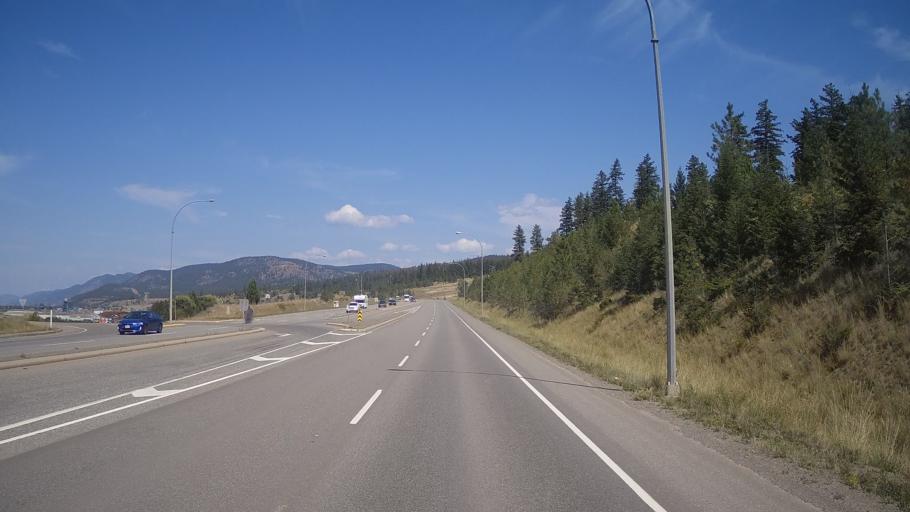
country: CA
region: British Columbia
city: Kamloops
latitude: 50.8320
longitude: -120.2800
